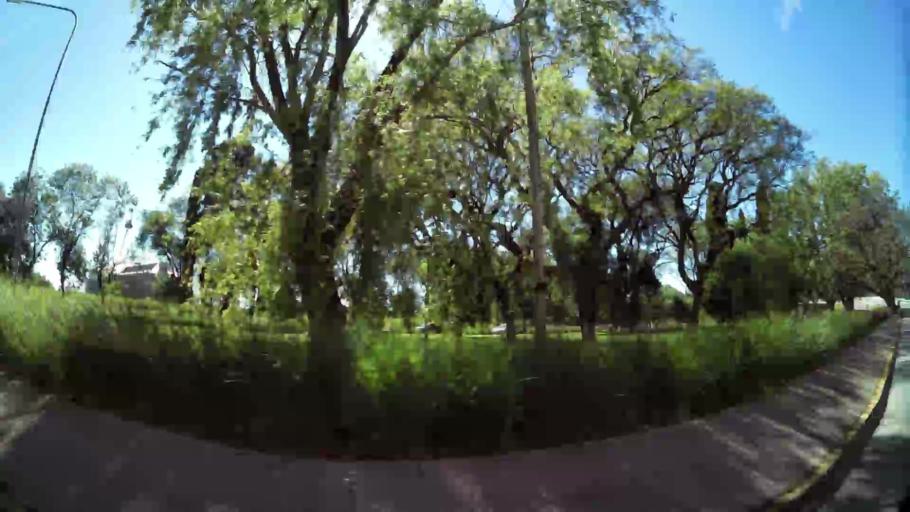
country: AR
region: Buenos Aires
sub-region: Partido de Vicente Lopez
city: Olivos
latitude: -34.5297
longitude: -58.4700
